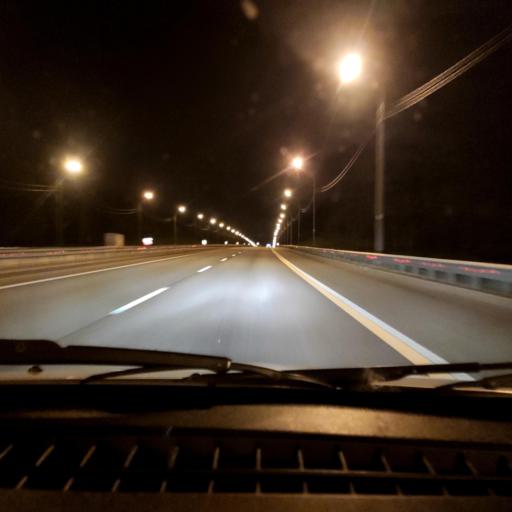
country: RU
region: Lipetsk
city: Zadonsk
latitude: 52.3932
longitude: 38.8630
